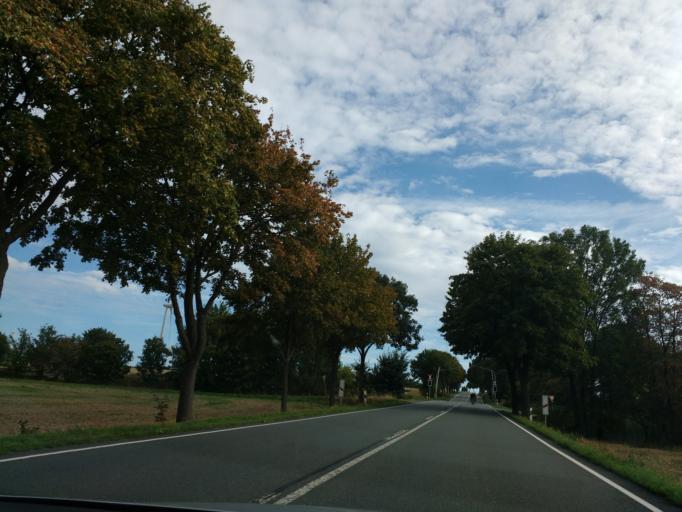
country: DE
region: North Rhine-Westphalia
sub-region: Regierungsbezirk Arnsberg
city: Anrochte
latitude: 51.5143
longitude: 8.3339
